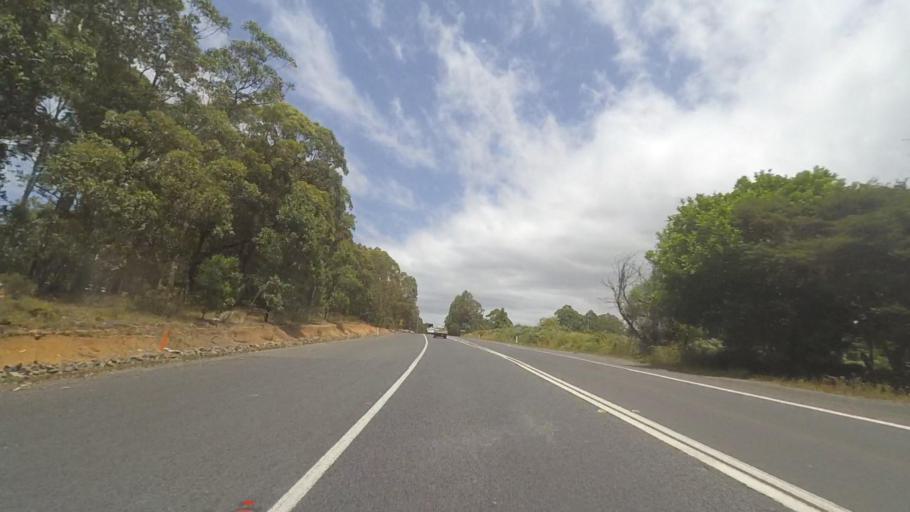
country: AU
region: New South Wales
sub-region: Shoalhaven Shire
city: Falls Creek
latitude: -35.0820
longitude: 150.5451
